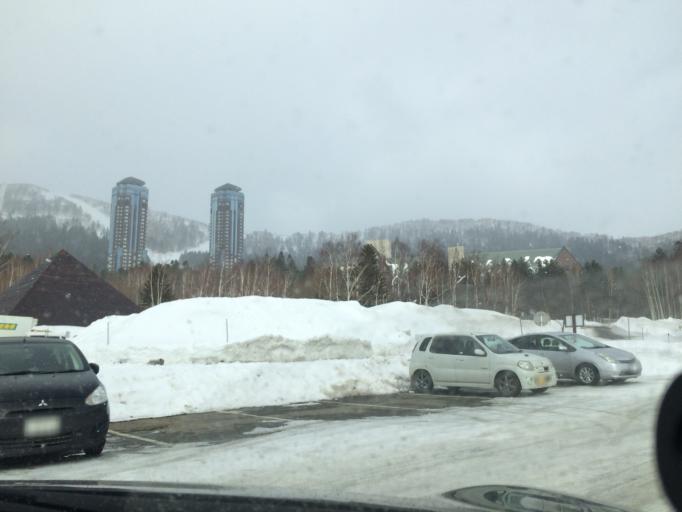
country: JP
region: Hokkaido
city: Shimo-furano
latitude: 43.0625
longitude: 142.6318
